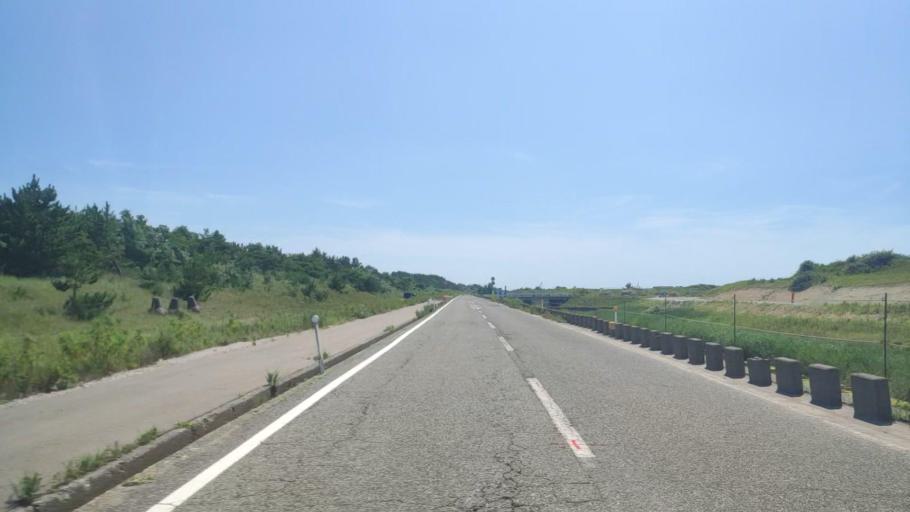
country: JP
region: Ishikawa
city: Kanazawa-shi
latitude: 36.6131
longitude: 136.5987
